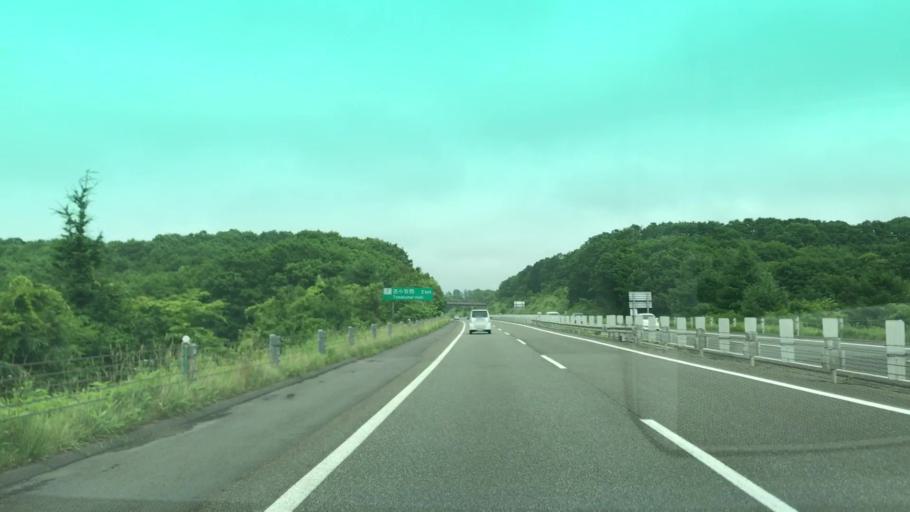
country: JP
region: Hokkaido
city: Tomakomai
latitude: 42.6180
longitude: 141.4739
